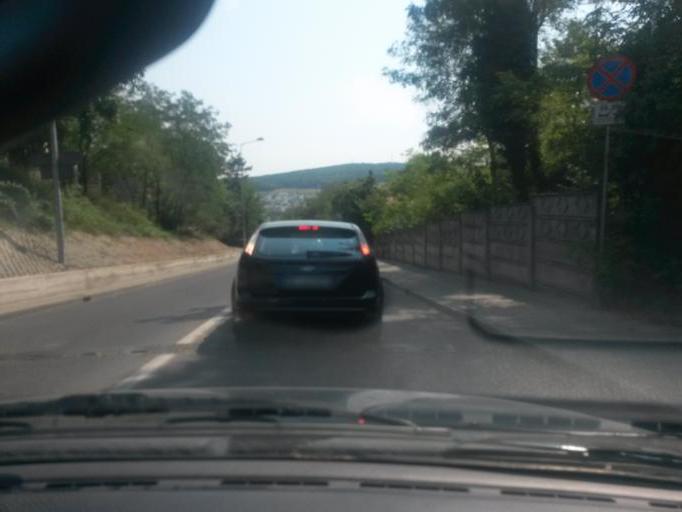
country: RO
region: Mures
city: Targu-Mures
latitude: 46.5414
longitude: 24.5732
